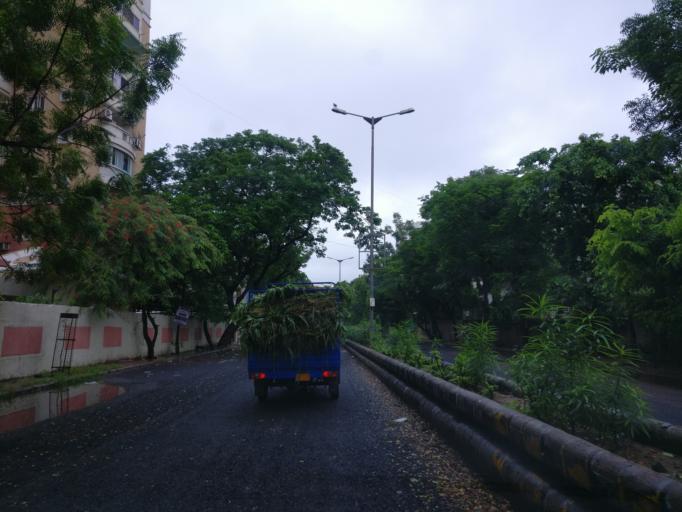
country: IN
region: Gujarat
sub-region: Ahmadabad
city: Sarkhej
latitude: 23.0200
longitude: 72.5083
